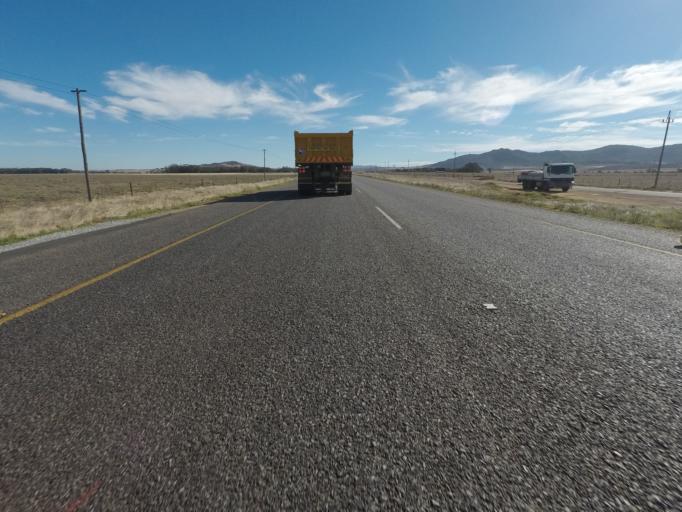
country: ZA
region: Western Cape
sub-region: West Coast District Municipality
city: Malmesbury
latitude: -33.6271
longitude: 18.7237
